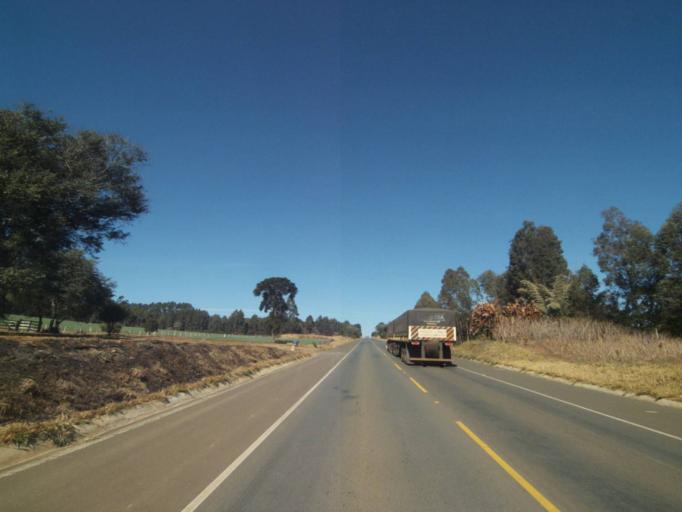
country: BR
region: Parana
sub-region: Tibagi
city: Tibagi
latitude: -24.5908
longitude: -50.4370
